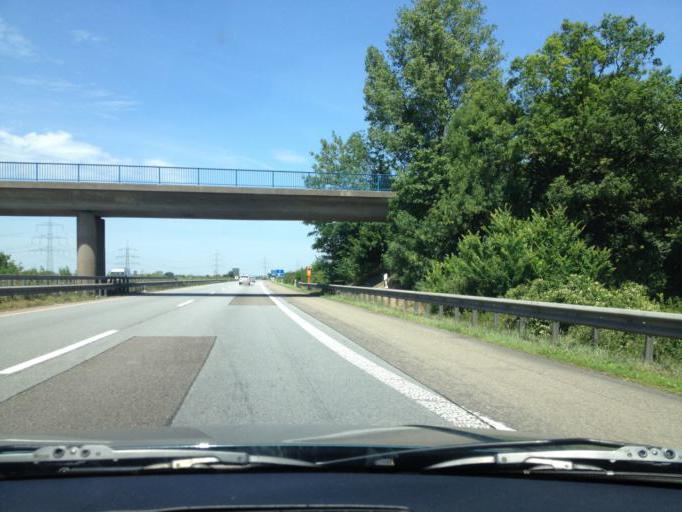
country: DE
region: Rheinland-Pfalz
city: Dannstadt-Schauernheim
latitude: 49.4476
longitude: 8.3207
